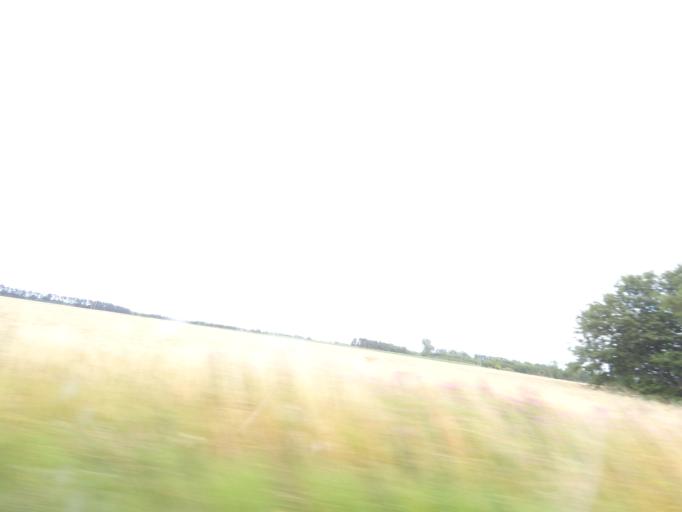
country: DK
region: South Denmark
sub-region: Nordfyns Kommune
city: Otterup
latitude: 55.4750
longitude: 10.3845
